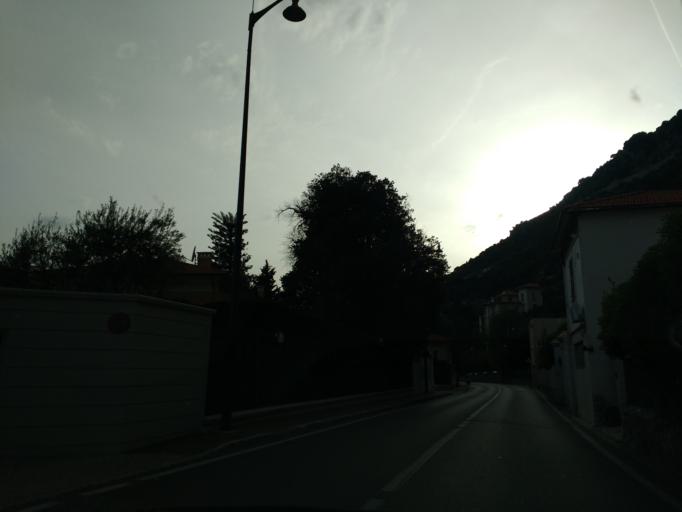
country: FR
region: Provence-Alpes-Cote d'Azur
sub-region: Departement des Alpes-Maritimes
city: Beaulieu-sur-Mer
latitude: 43.7135
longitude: 7.3403
